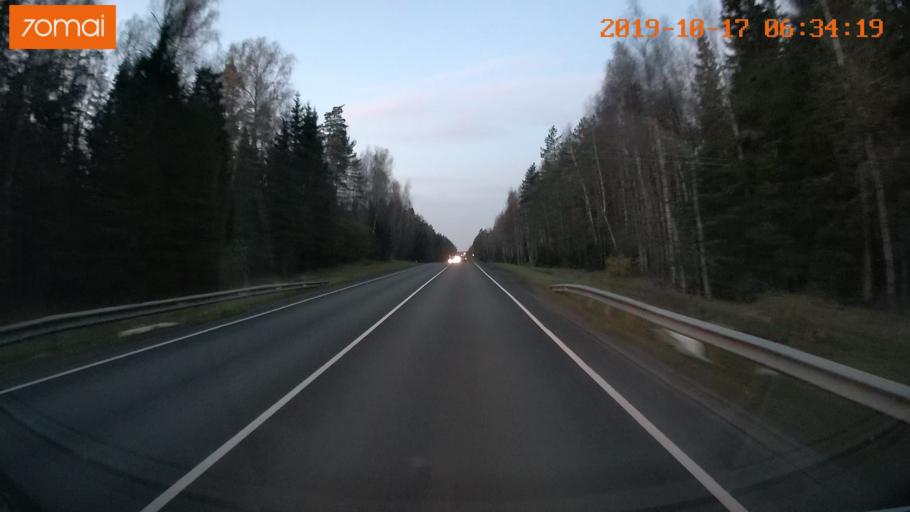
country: RU
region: Ivanovo
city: Novoye Leushino
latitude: 56.7045
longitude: 40.6406
